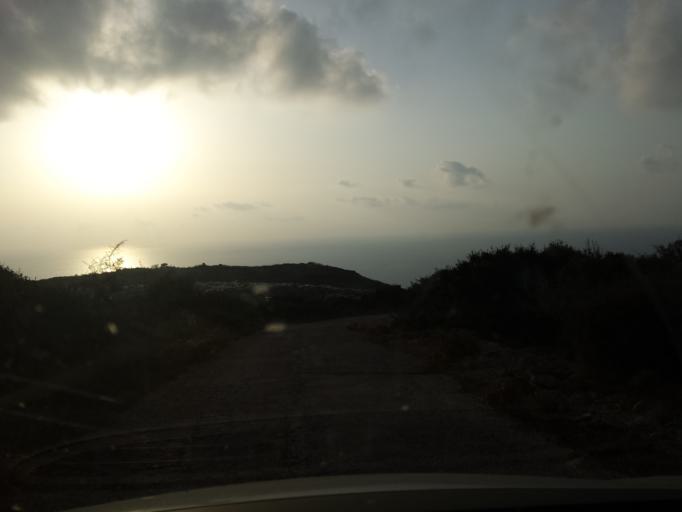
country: GR
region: Peloponnese
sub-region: Nomos Messinias
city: Pylos
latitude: 36.8854
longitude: 21.6871
